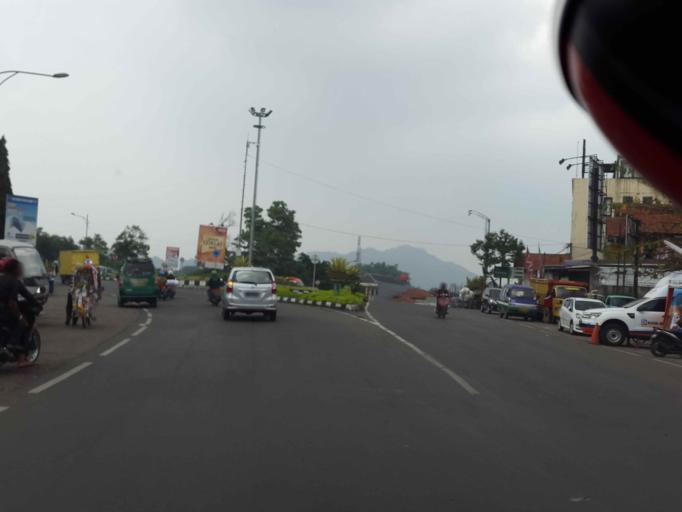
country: ID
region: West Java
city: Cimahi
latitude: -6.9028
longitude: 107.5363
